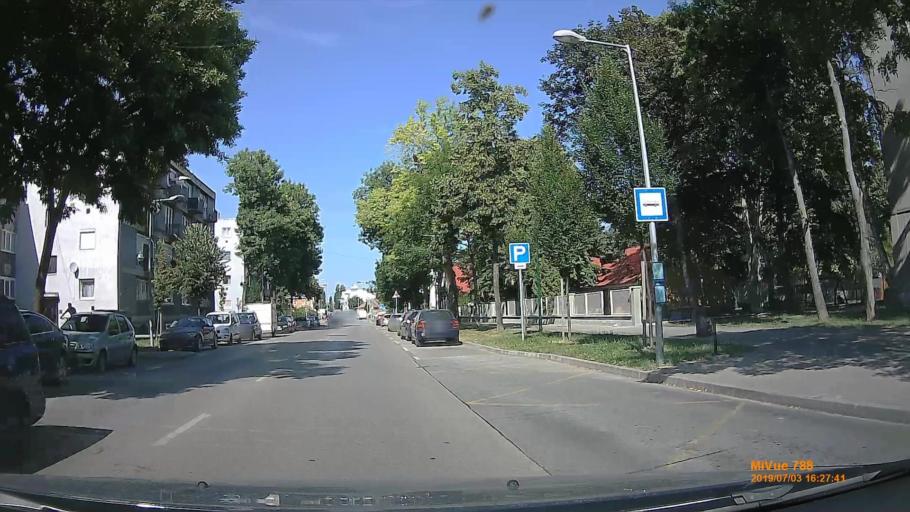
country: HU
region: Gyor-Moson-Sopron
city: Gyor
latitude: 47.6874
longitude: 17.6194
